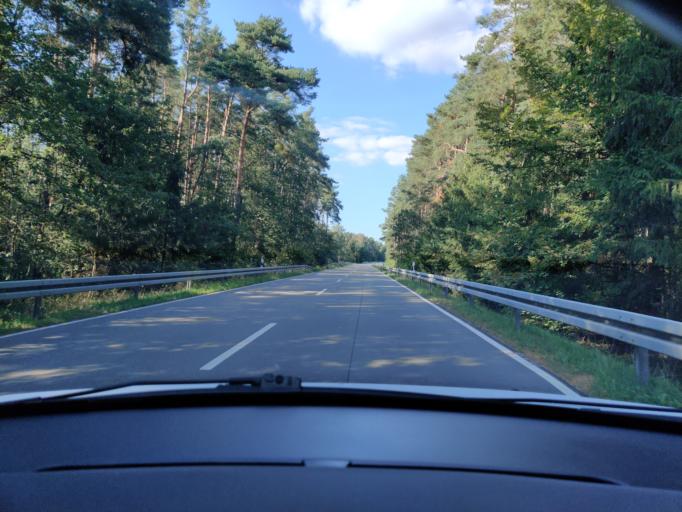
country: DE
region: Bavaria
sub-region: Upper Palatinate
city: Schwarzenfeld
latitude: 49.3513
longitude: 12.1462
